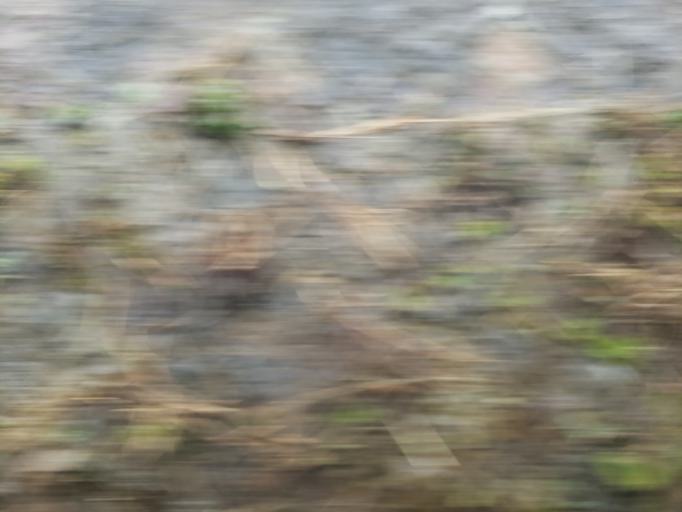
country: JP
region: Hyogo
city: Kobe
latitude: 34.6359
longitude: 135.0959
